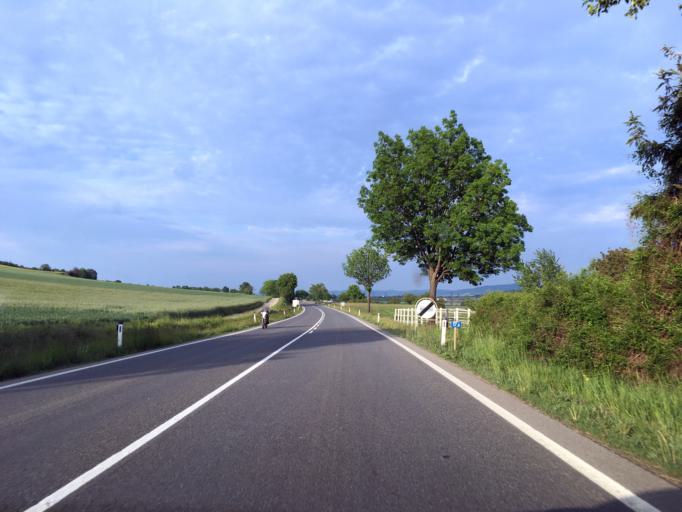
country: AT
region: Lower Austria
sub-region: Politischer Bezirk Tulln
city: Sieghartskirchen
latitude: 48.2746
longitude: 15.9872
